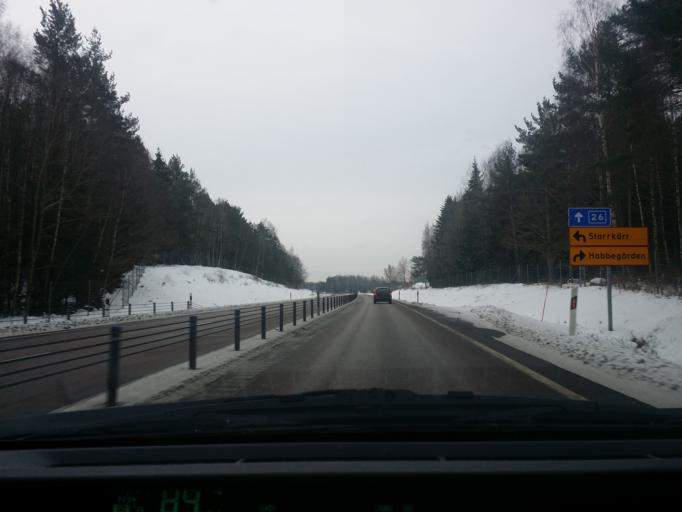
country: SE
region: Vaestra Goetaland
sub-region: Skovde Kommun
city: Stopen
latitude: 58.5359
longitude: 13.8136
